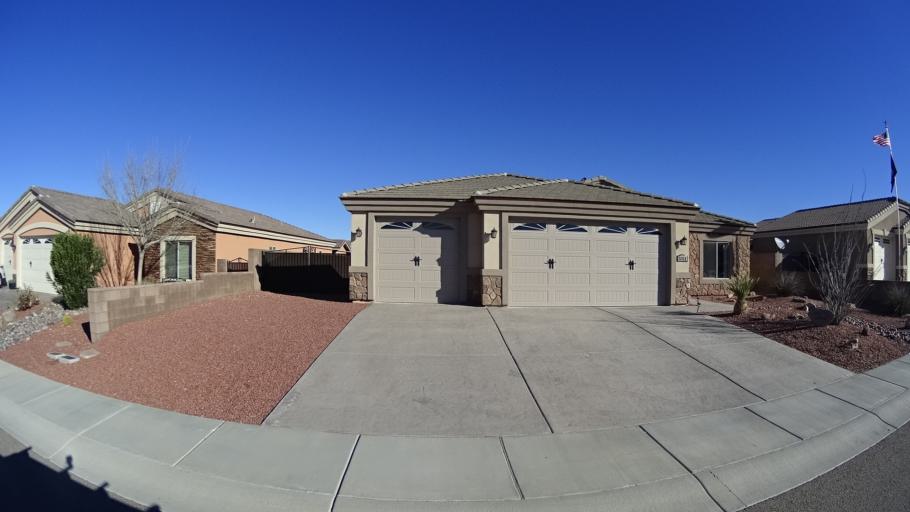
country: US
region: Arizona
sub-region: Mohave County
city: Kingman
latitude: 35.1878
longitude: -113.9998
